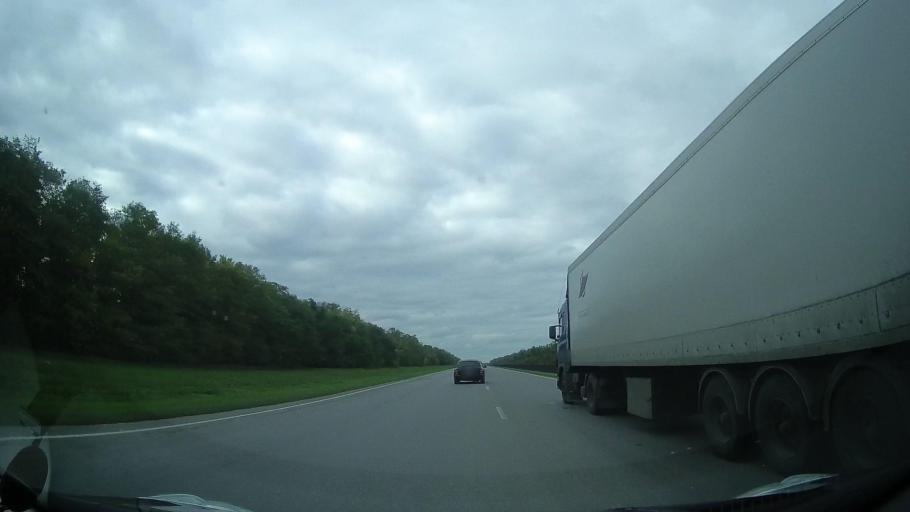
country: RU
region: Rostov
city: Yegorlykskaya
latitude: 46.6305
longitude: 40.5882
